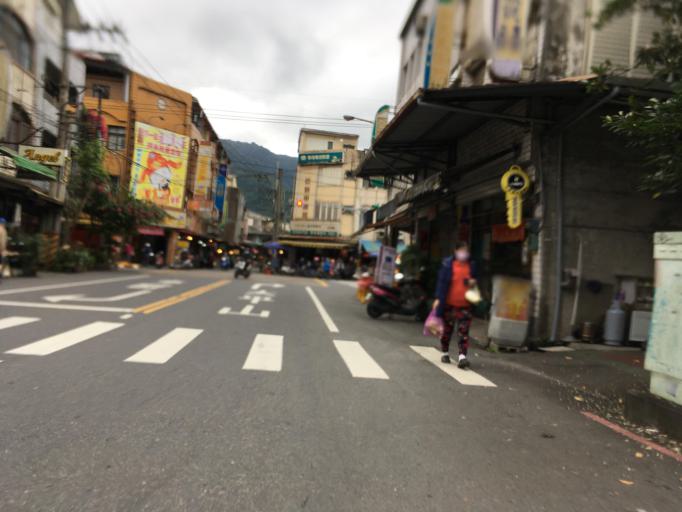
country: TW
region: Taiwan
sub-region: Yilan
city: Yilan
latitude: 24.6665
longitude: 121.6524
